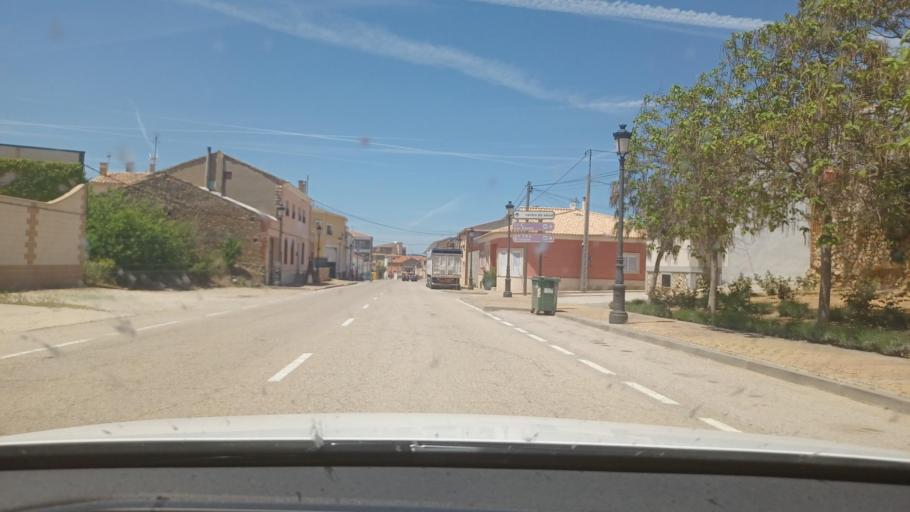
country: ES
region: Castille-La Mancha
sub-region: Provincia de Cuenca
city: Villares del Saz
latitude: 39.8383
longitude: -2.5015
